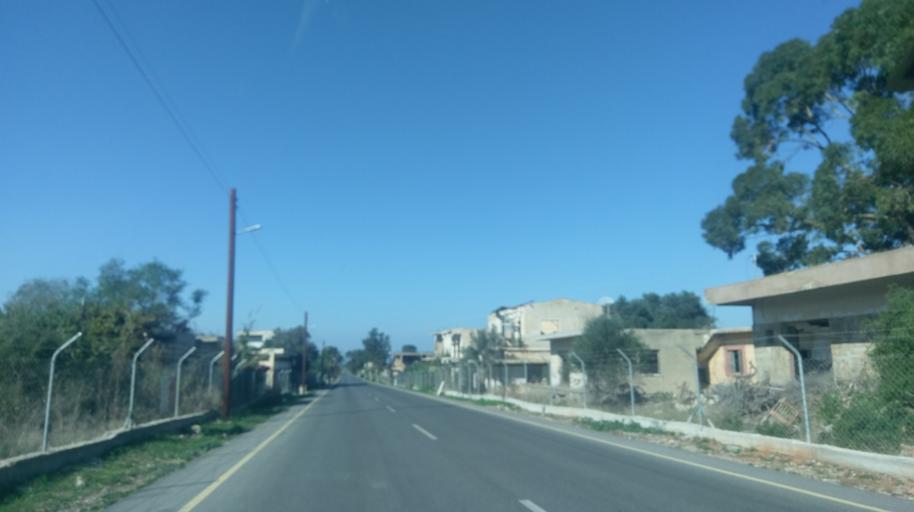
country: CY
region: Ammochostos
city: Deryneia
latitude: 35.0771
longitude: 33.9587
